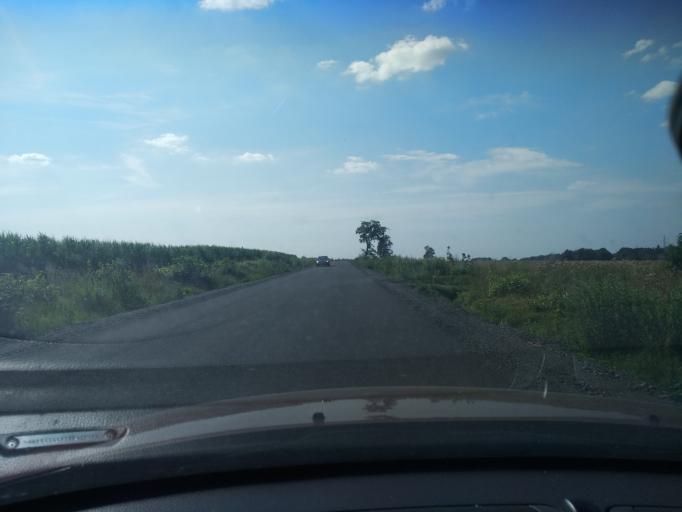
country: PL
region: Lower Silesian Voivodeship
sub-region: Powiat lubanski
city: Lesna
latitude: 51.0452
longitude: 15.2008
